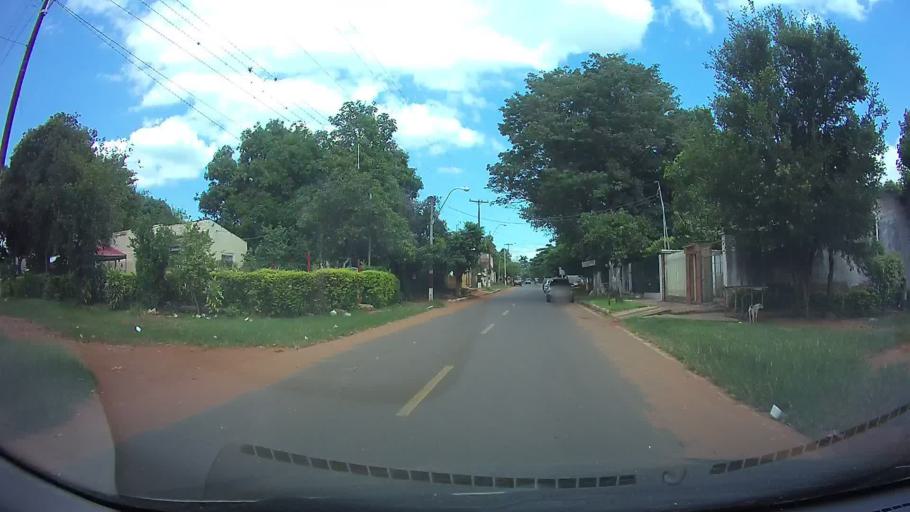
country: PY
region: Central
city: Aregua
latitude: -25.2915
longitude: -57.4286
